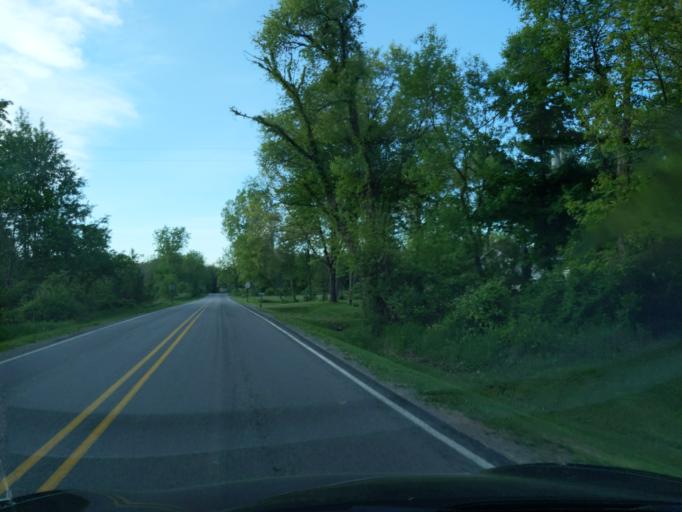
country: US
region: Michigan
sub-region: Ingham County
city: Leslie
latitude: 42.4788
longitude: -84.3170
